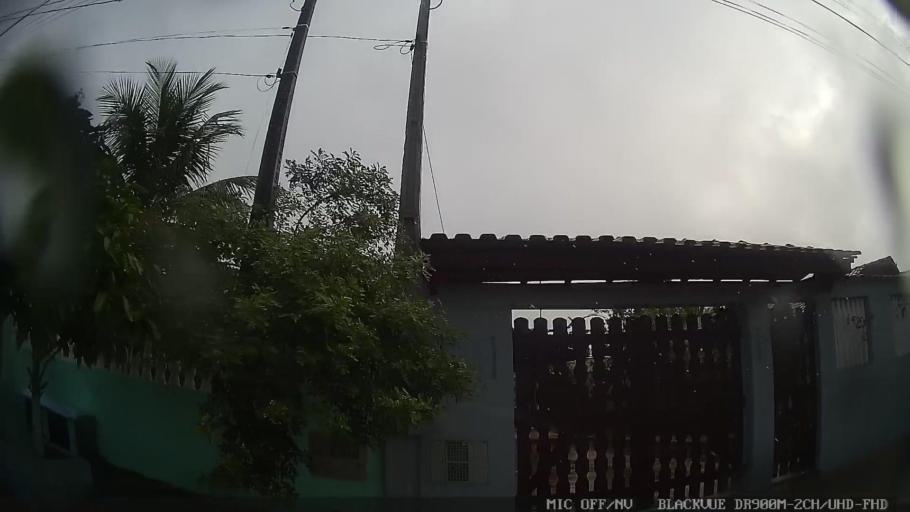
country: BR
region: Sao Paulo
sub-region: Itanhaem
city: Itanhaem
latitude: -24.2376
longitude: -46.9022
